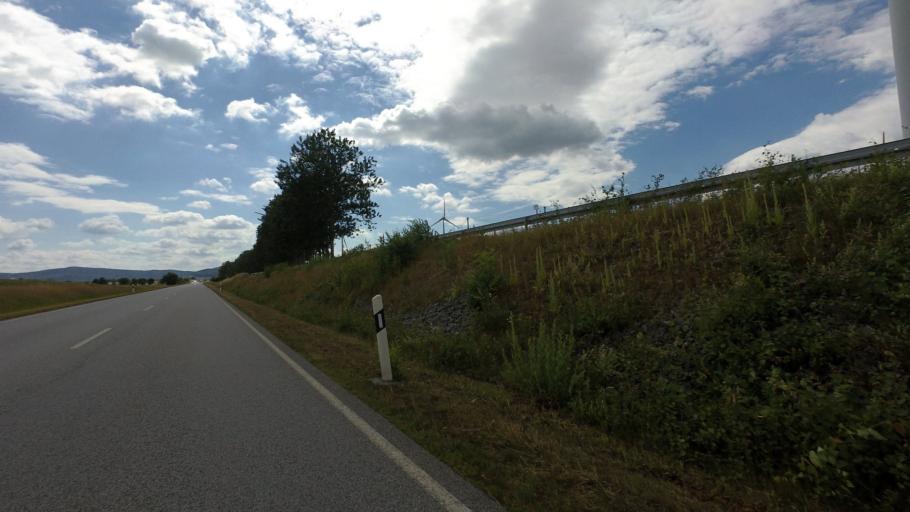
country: DE
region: Saxony
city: Nebelschutz
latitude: 51.2369
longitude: 14.1598
